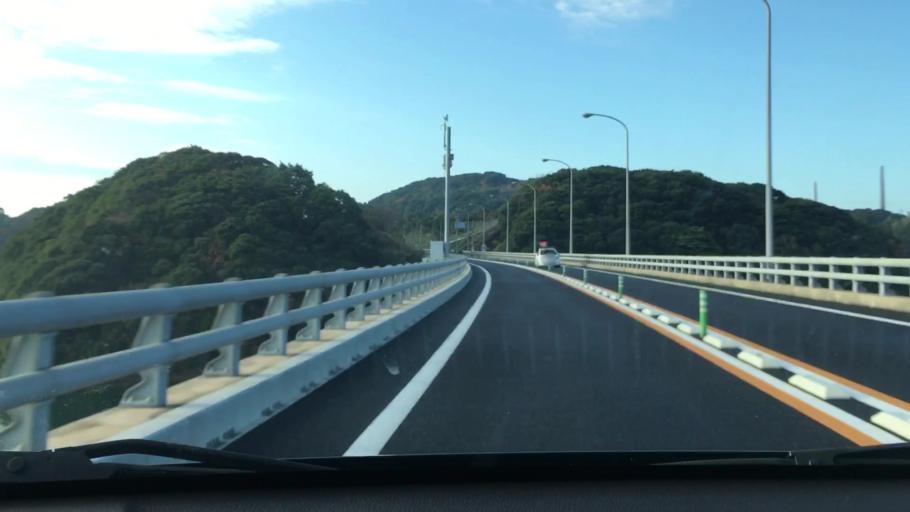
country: JP
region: Nagasaki
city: Sasebo
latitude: 33.0757
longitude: 129.7684
